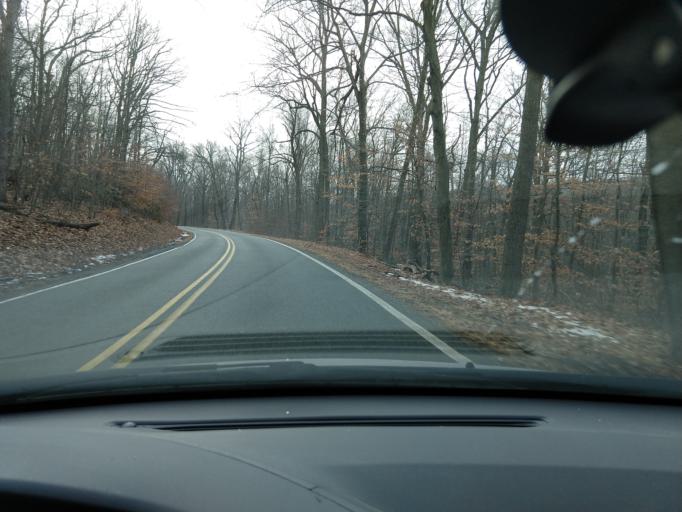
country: US
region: Pennsylvania
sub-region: Berks County
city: Birdsboro
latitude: 40.2277
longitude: -75.7747
